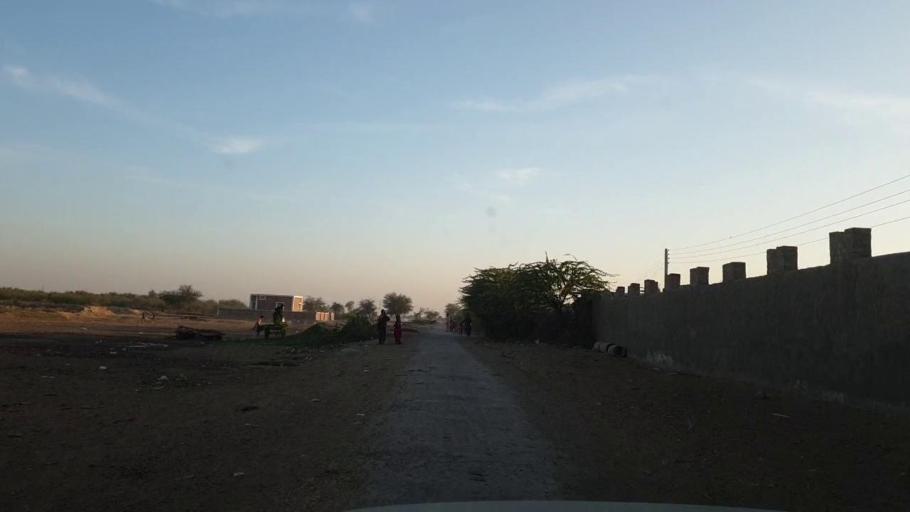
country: PK
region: Sindh
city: Kunri
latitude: 25.1302
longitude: 69.4286
